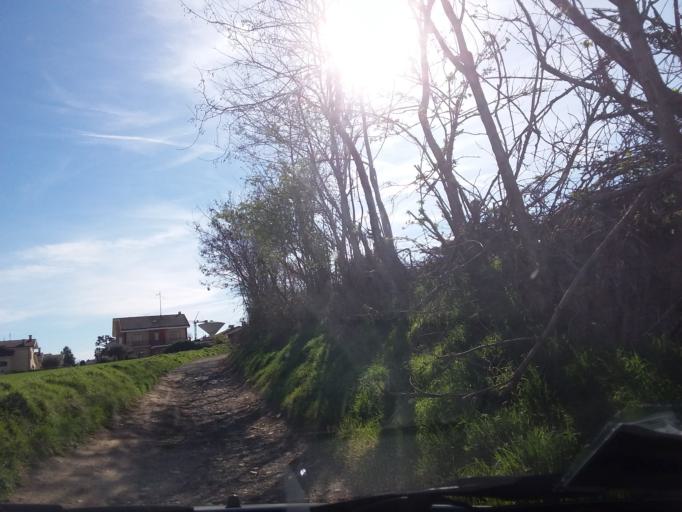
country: IT
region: Piedmont
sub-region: Provincia di Torino
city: Rivoli
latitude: 45.0783
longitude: 7.5381
